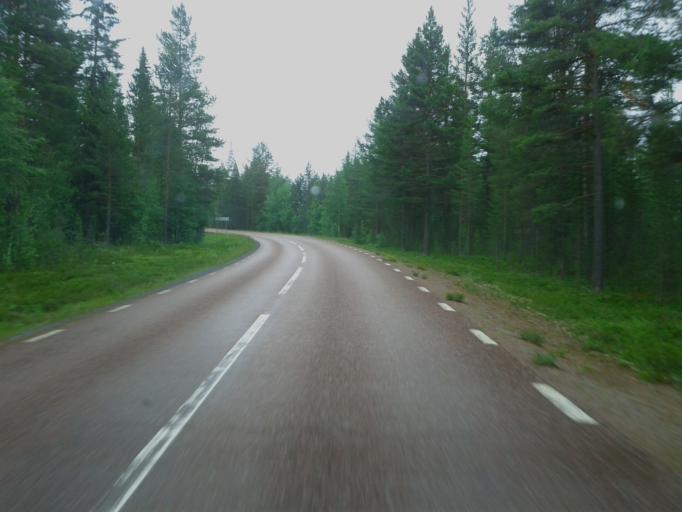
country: NO
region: Hedmark
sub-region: Trysil
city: Innbygda
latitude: 61.7873
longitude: 12.9303
